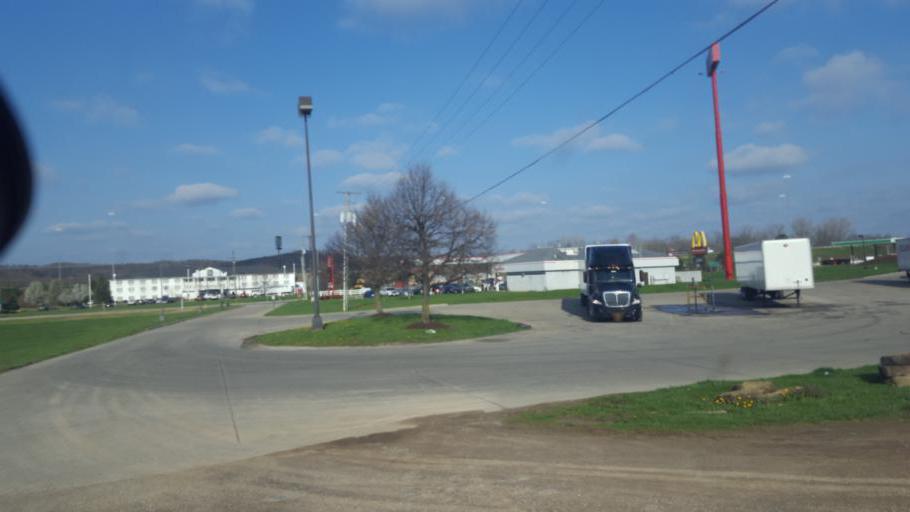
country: US
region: Ohio
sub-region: Sandusky County
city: Bellville
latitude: 40.6472
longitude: -82.5421
